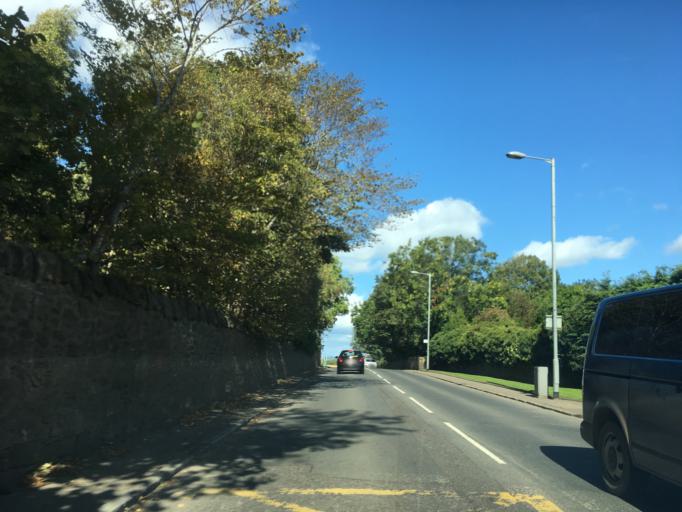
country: GB
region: Scotland
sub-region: West Lothian
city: Seafield
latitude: 55.9322
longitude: -3.1138
